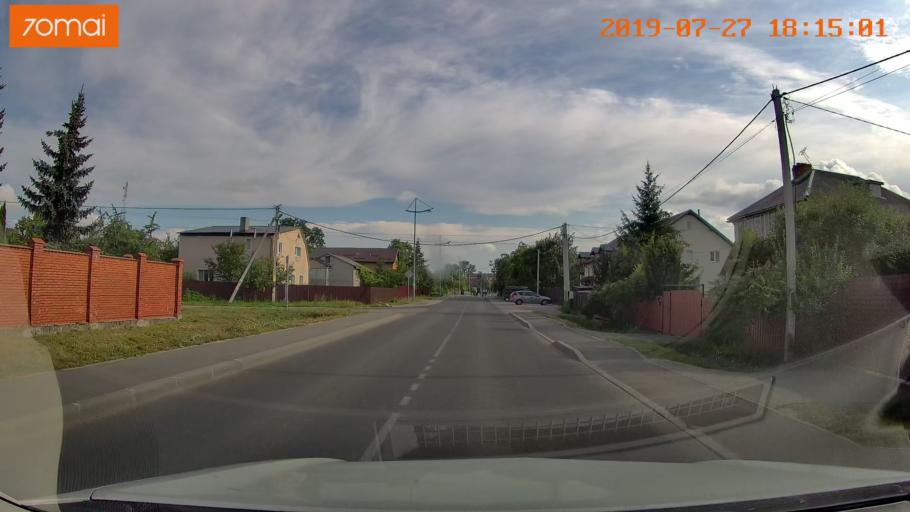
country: RU
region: Kaliningrad
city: Bol'shoe Isakovo
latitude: 54.7224
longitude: 20.6006
